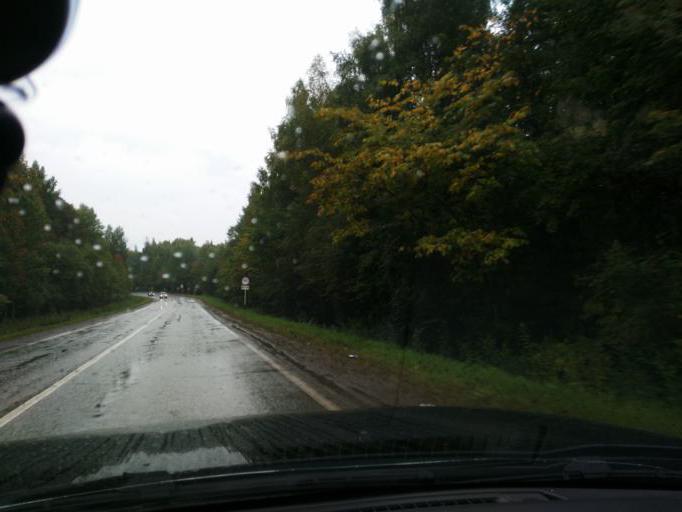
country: RU
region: Perm
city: Yugo-Kamskiy
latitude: 57.5028
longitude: 55.6882
